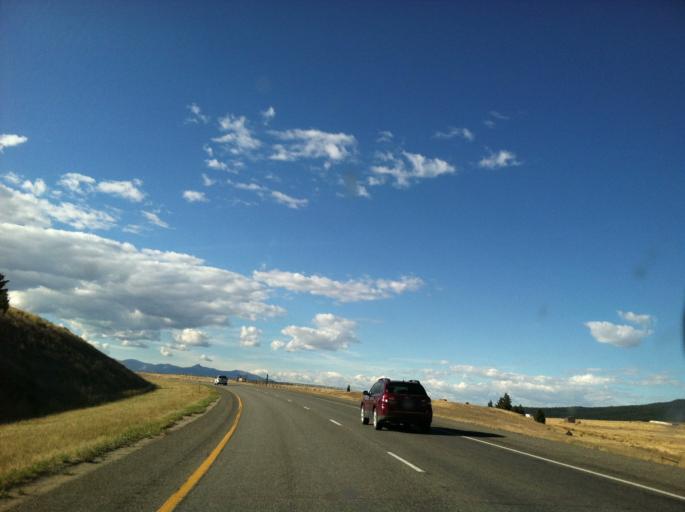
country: US
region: Montana
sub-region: Deer Lodge County
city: Warm Springs
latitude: 46.0378
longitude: -112.7335
